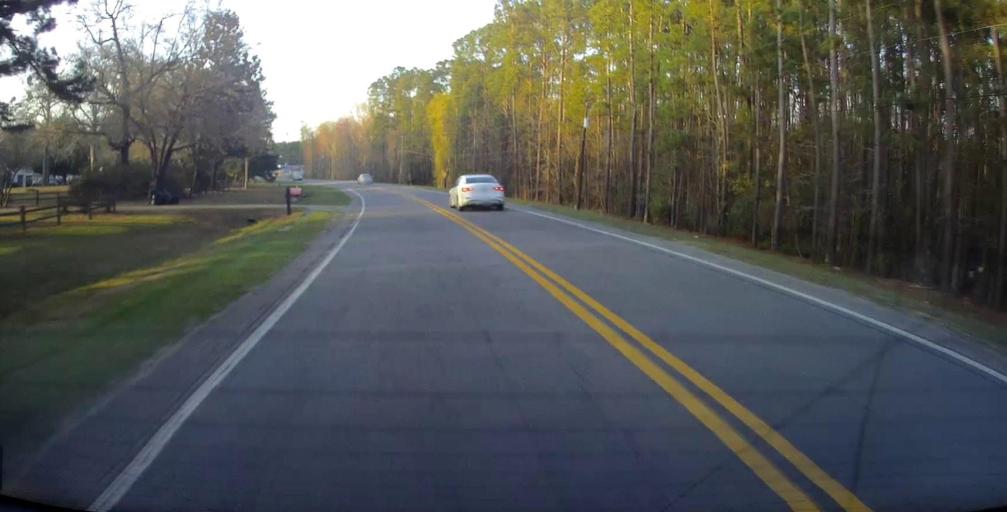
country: US
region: Georgia
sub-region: Chatham County
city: Bloomingdale
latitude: 32.1651
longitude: -81.3849
